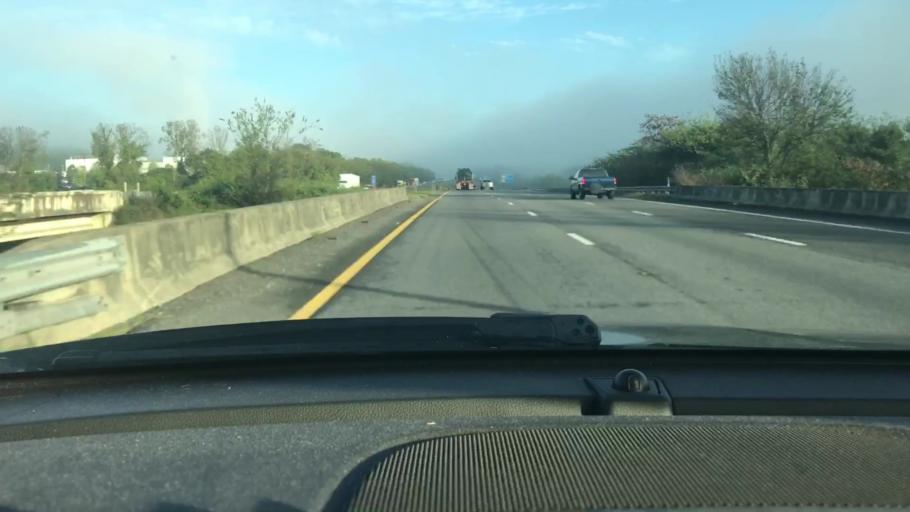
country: US
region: Tennessee
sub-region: Davidson County
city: Goodlettsville
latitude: 36.3258
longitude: -86.7059
